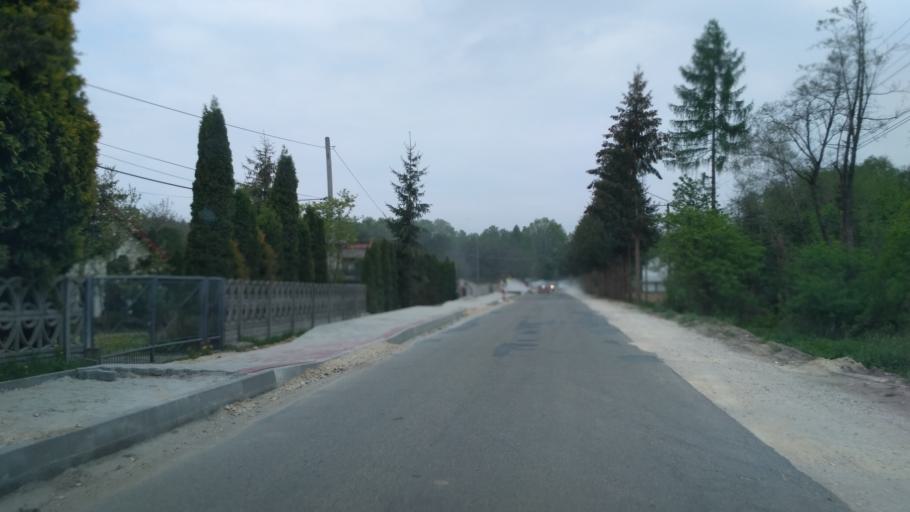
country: PL
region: Lesser Poland Voivodeship
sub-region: Powiat tarnowski
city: Skrzyszow
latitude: 49.9826
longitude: 21.0638
